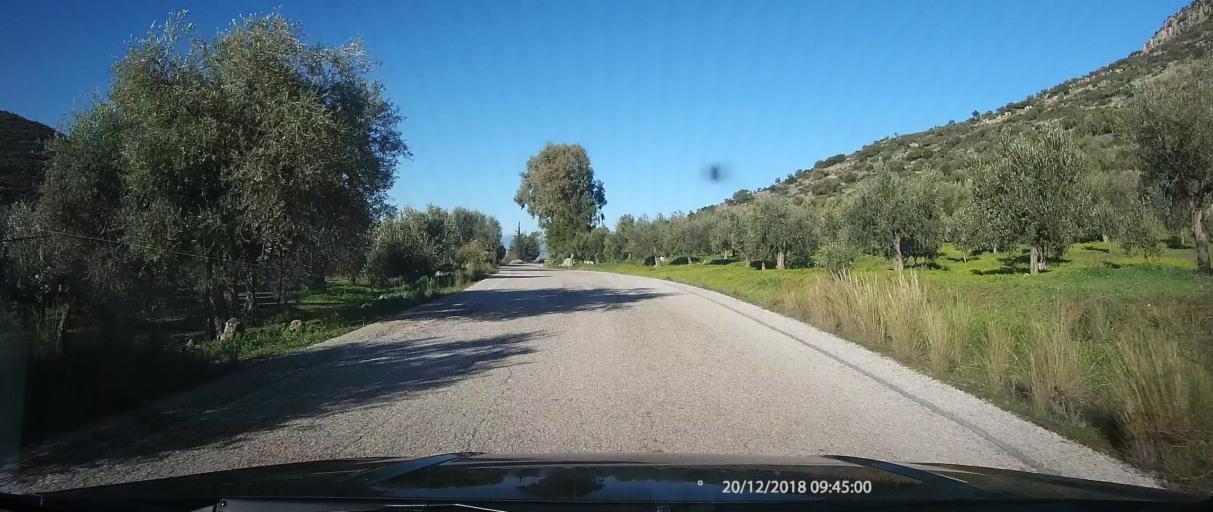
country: GR
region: Peloponnese
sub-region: Nomos Lakonias
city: Yerakion
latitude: 36.9814
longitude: 22.7336
